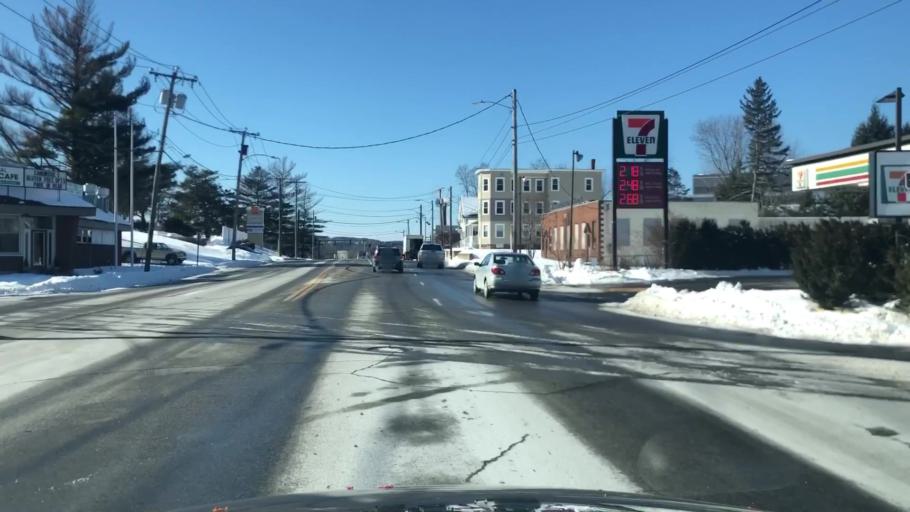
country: US
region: New Hampshire
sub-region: Hillsborough County
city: Manchester
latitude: 42.9736
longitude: -71.4657
